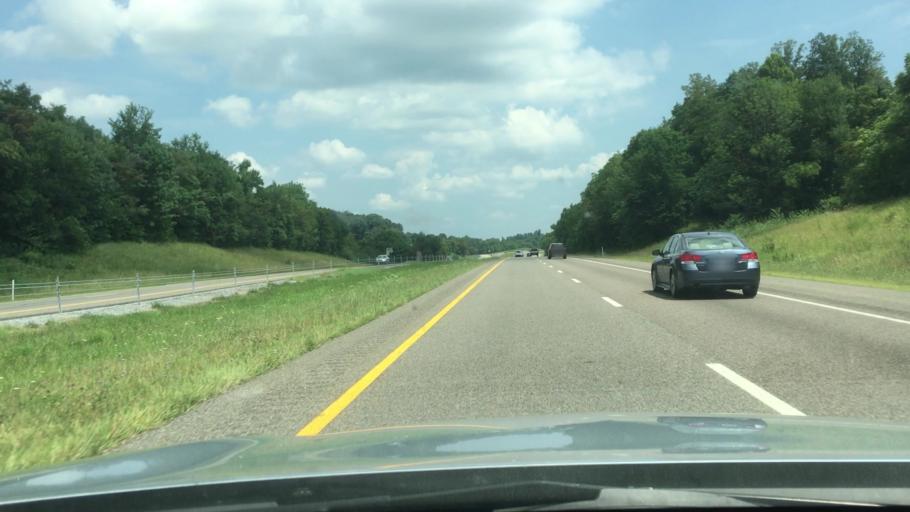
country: US
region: Tennessee
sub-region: Carter County
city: Pine Crest
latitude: 36.2600
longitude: -82.3224
